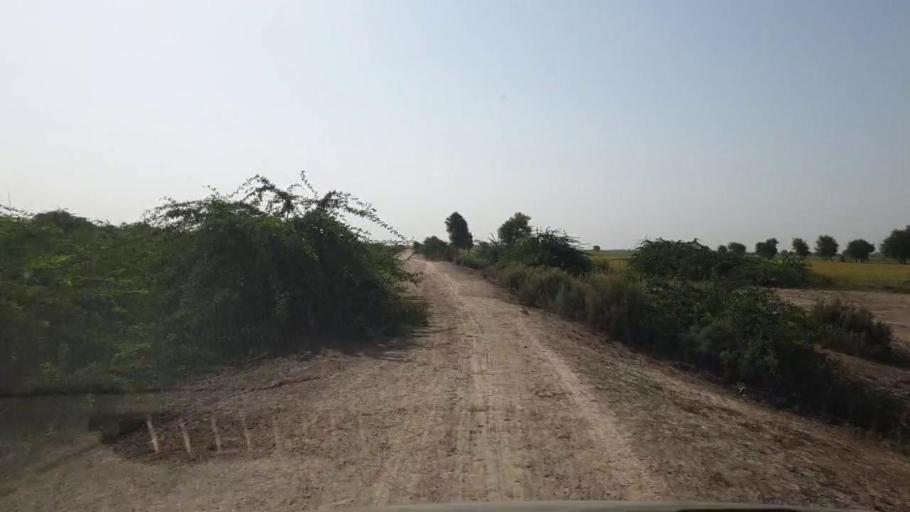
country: PK
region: Sindh
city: Kadhan
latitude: 24.5728
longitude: 69.0820
